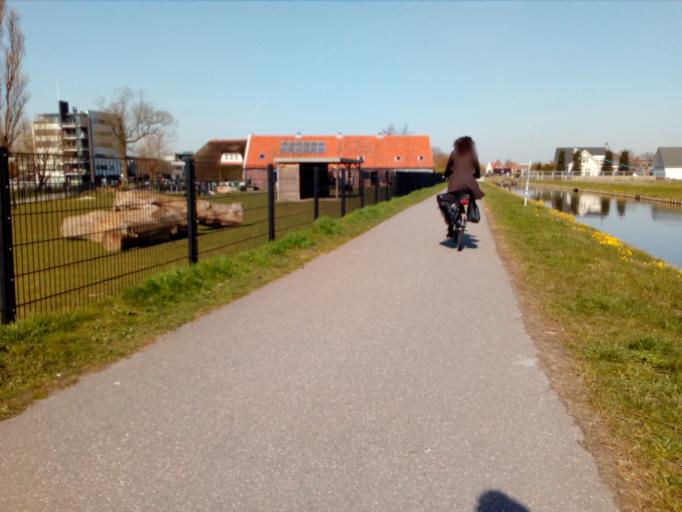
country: NL
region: South Holland
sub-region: Gemeente Rijswijk
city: Rijswijk
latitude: 52.0262
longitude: 4.3006
